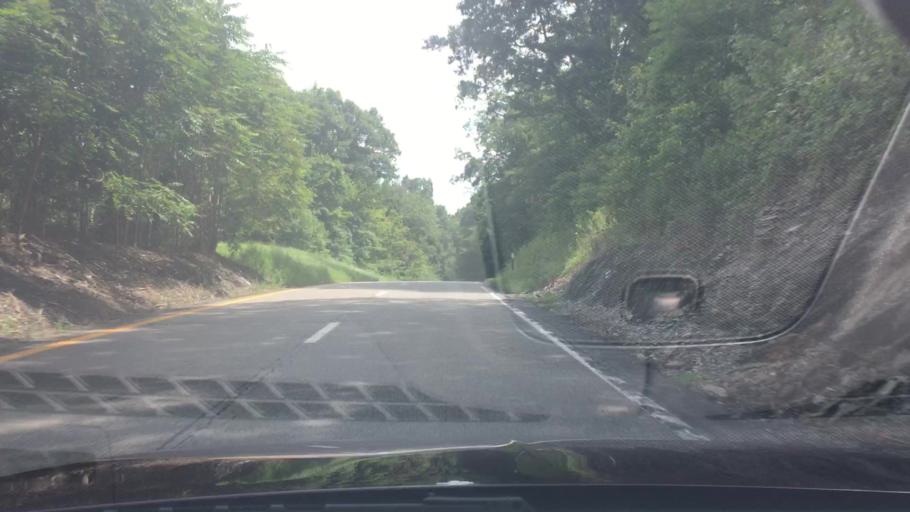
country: US
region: New York
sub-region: Dutchess County
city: Hillside Lake
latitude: 41.6208
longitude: -73.7674
